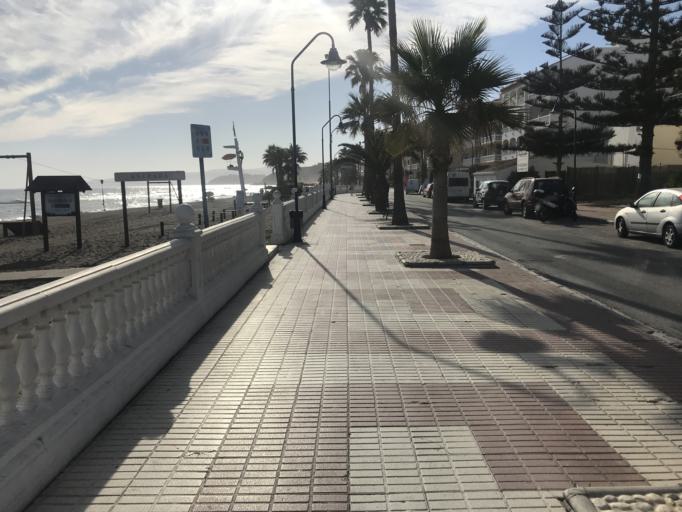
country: ES
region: Andalusia
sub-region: Provincia de Malaga
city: Torrox
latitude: 36.7378
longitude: -3.9916
